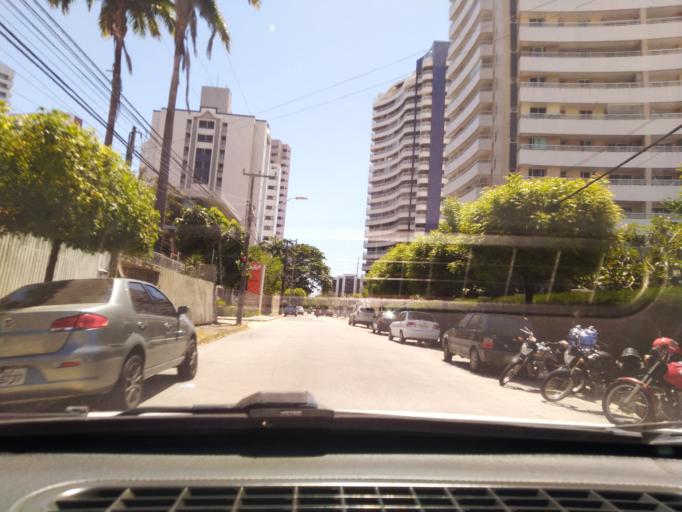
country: BR
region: Ceara
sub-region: Fortaleza
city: Fortaleza
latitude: -3.7439
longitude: -38.4772
